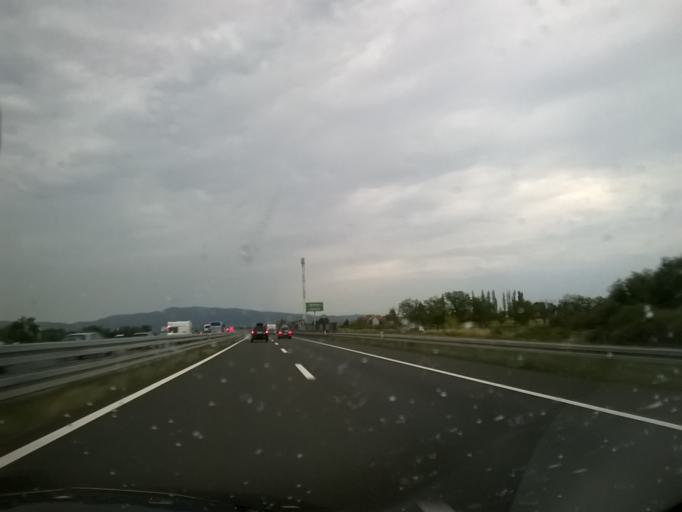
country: HR
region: Grad Zagreb
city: Brezovica
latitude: 45.7309
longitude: 15.8748
